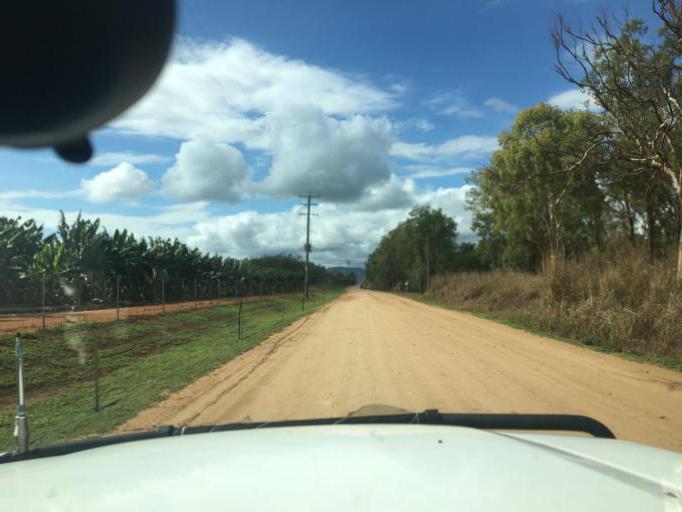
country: AU
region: Queensland
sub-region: Tablelands
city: Mareeba
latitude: -17.0966
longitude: 145.4121
